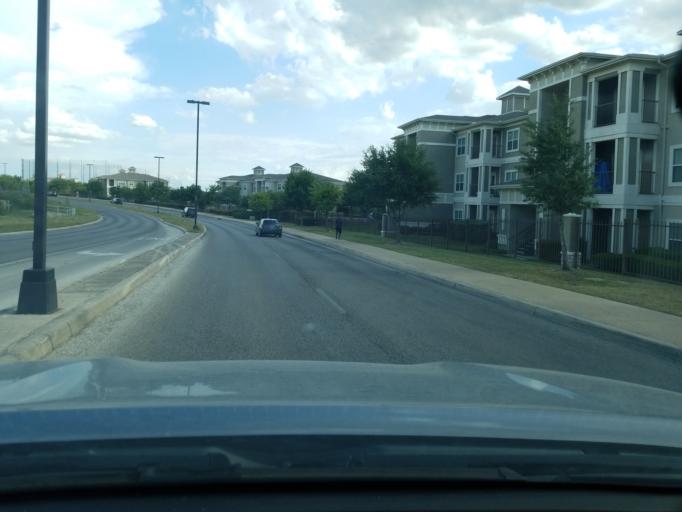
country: US
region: Texas
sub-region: Bexar County
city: Shavano Park
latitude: 29.6010
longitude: -98.5969
